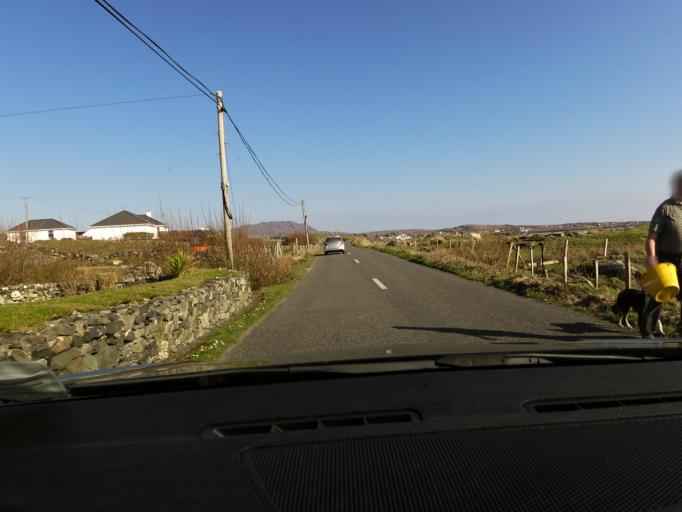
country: IE
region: Connaught
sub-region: County Galway
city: Clifden
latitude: 53.4146
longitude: -10.0478
